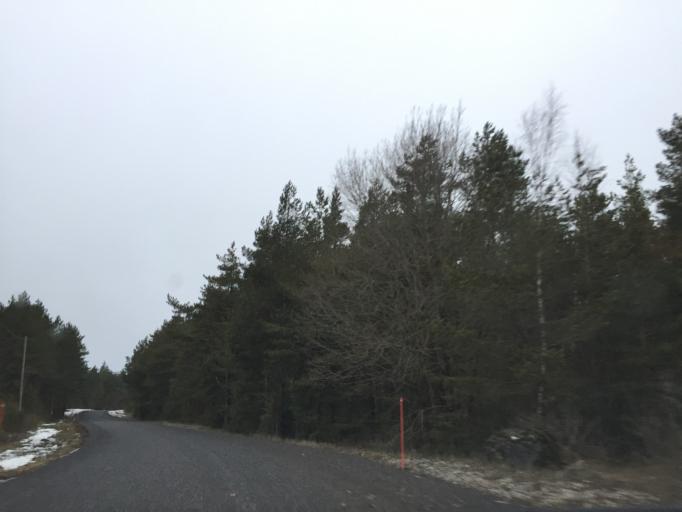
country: EE
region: Laeaene
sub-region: Lihula vald
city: Lihula
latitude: 58.6586
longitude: 23.5858
